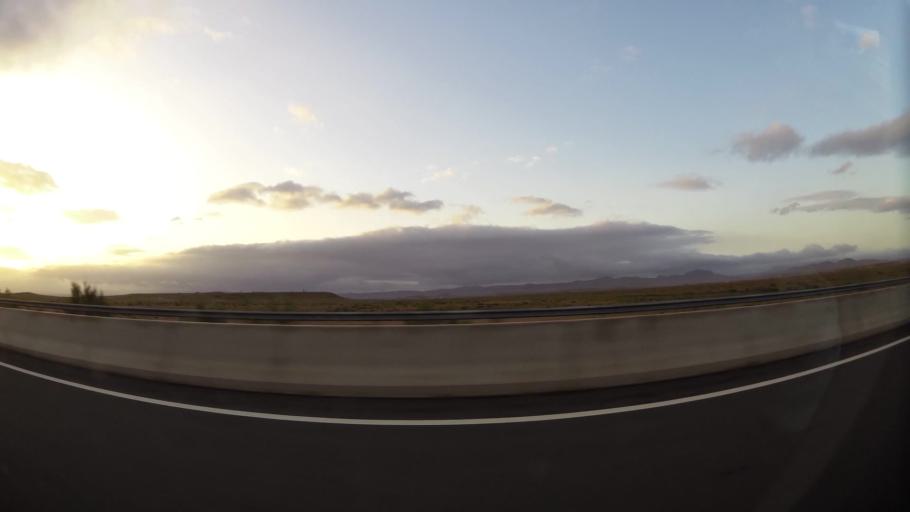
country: MA
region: Oriental
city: Taourirt
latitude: 34.5488
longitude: -2.8879
